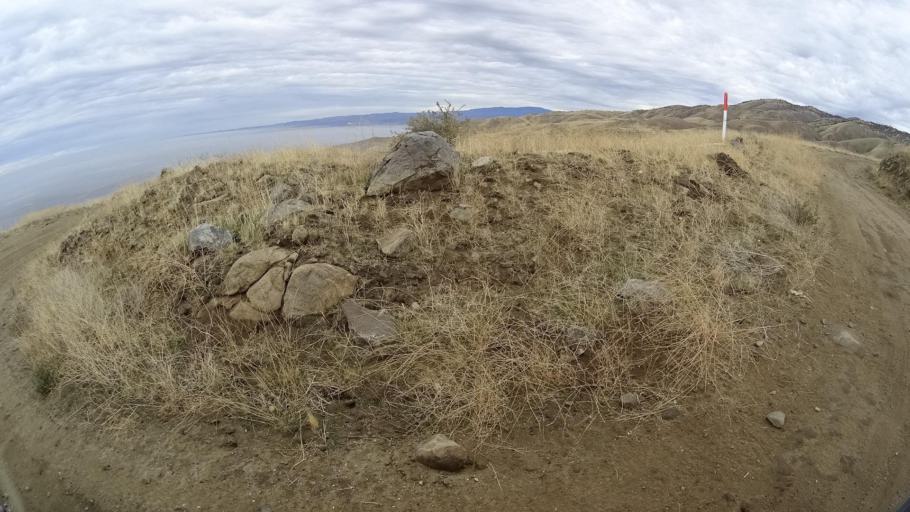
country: US
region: California
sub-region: Kern County
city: Arvin
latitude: 35.1359
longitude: -118.7802
